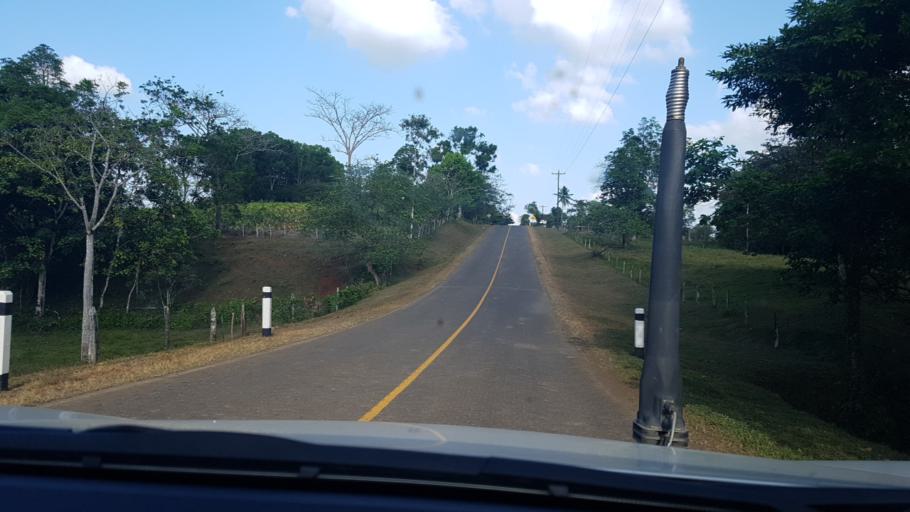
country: NI
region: Atlantico Sur
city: Nueva Guinea
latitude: 11.6953
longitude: -84.4123
